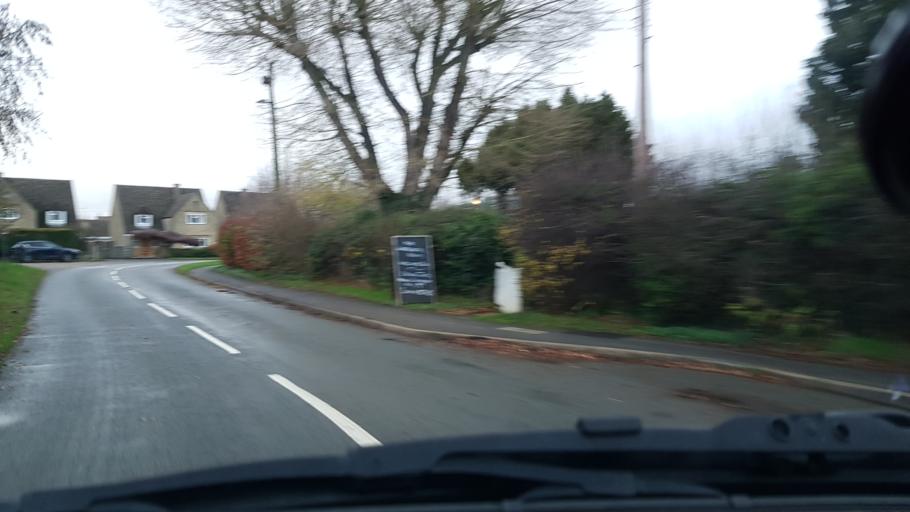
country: GB
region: England
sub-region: Gloucestershire
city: Winchcombe
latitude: 51.9982
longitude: -2.0023
